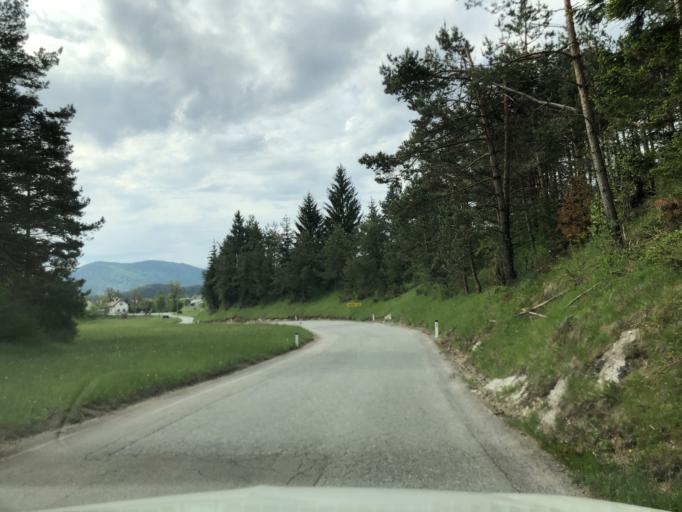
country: SI
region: Bloke
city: Nova Vas
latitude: 45.7808
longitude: 14.5021
